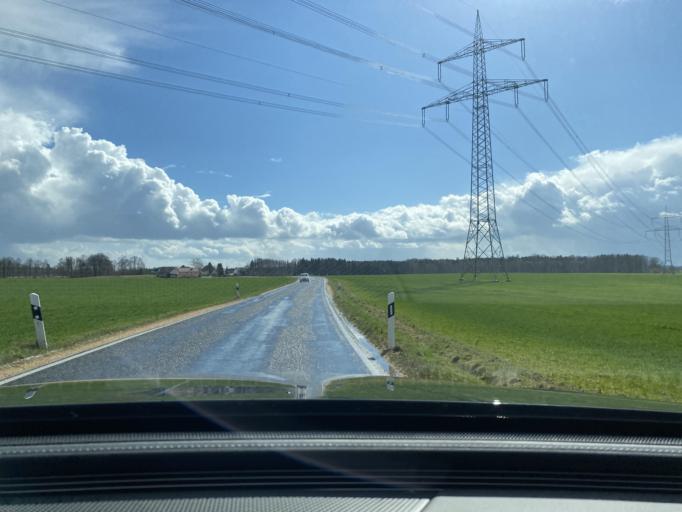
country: DE
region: Saxony
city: Radibor
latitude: 51.2673
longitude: 14.4296
